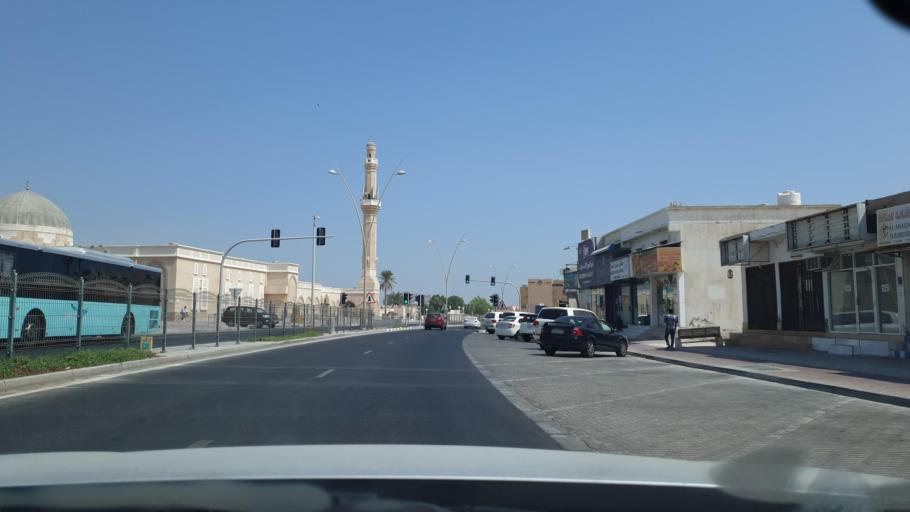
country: QA
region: Al Khawr
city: Al Khawr
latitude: 25.6840
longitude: 51.5058
